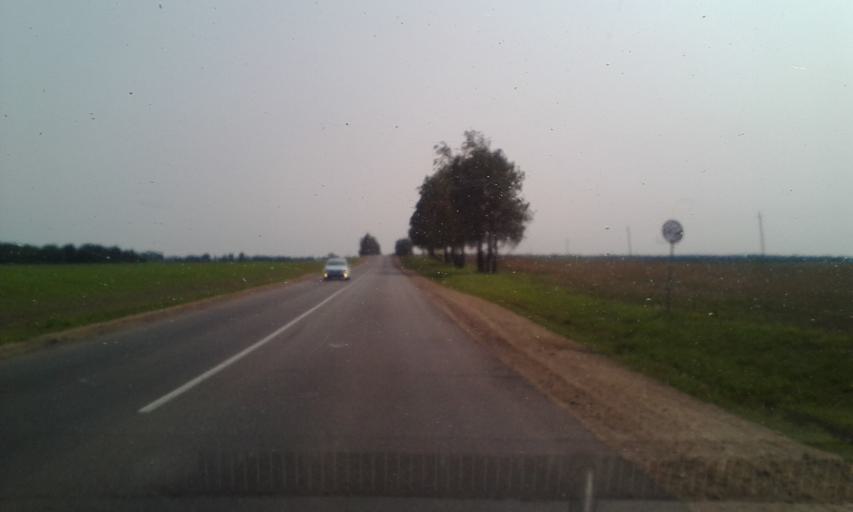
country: BY
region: Minsk
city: Hatava
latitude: 53.8259
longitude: 27.6241
